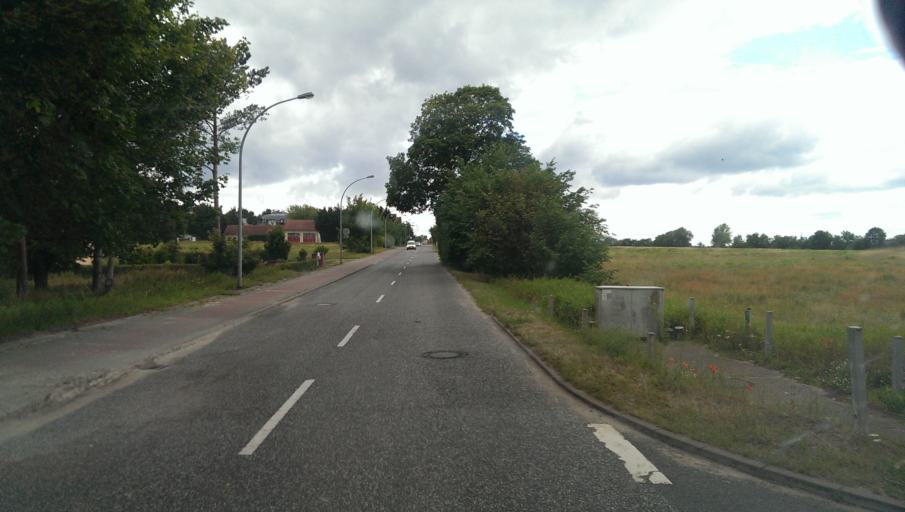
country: DE
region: Brandenburg
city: Stahnsdorf
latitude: 52.3666
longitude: 13.2084
